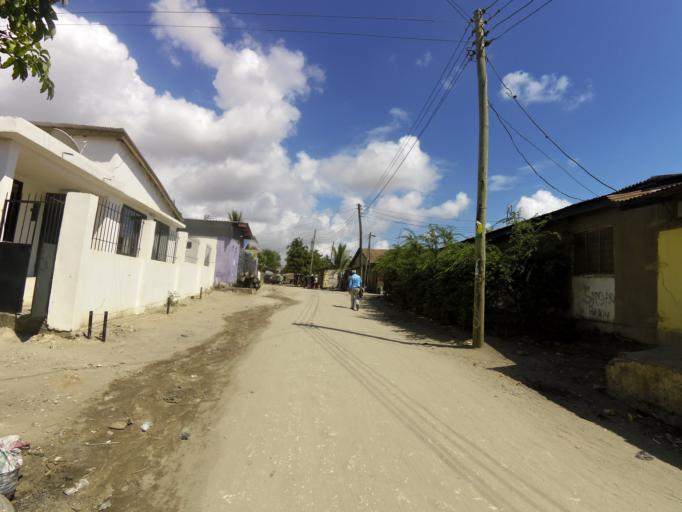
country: TZ
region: Dar es Salaam
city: Magomeni
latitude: -6.7888
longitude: 39.2570
